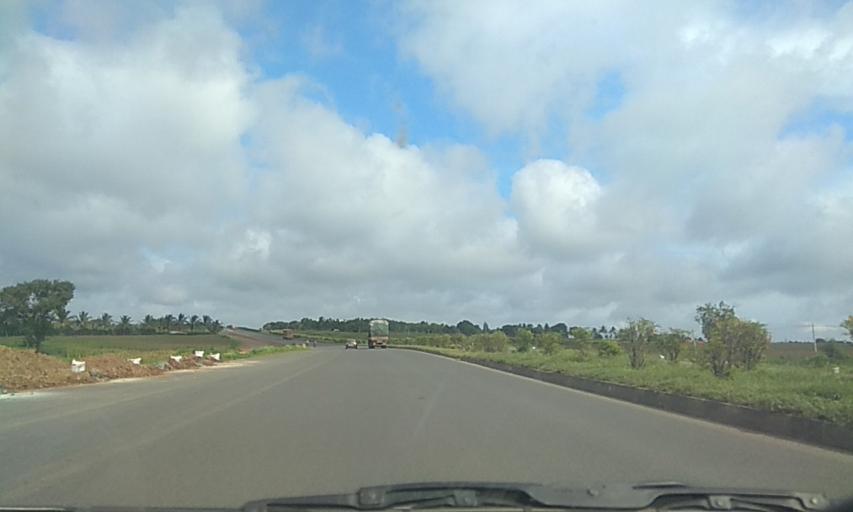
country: IN
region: Karnataka
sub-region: Haveri
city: Shiggaon
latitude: 15.0038
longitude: 75.2045
